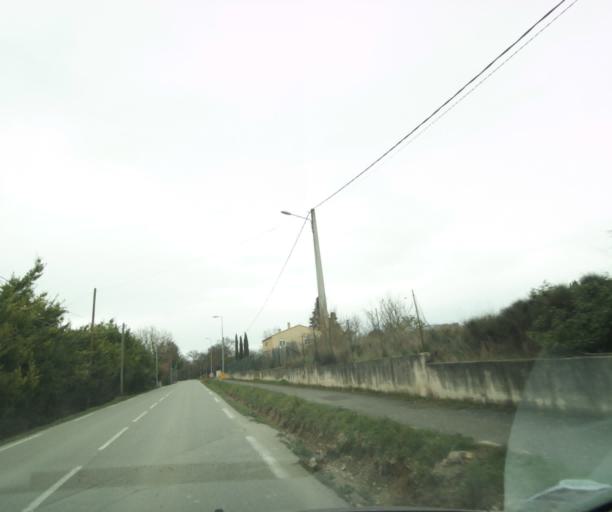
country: FR
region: Provence-Alpes-Cote d'Azur
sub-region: Departement des Bouches-du-Rhone
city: Aix-en-Provence
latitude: 43.5754
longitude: 5.4156
